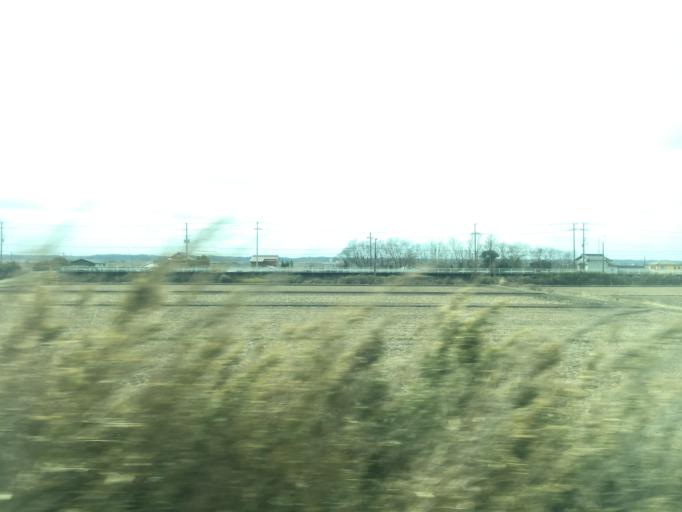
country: JP
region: Chiba
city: Narita
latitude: 35.8215
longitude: 140.2649
